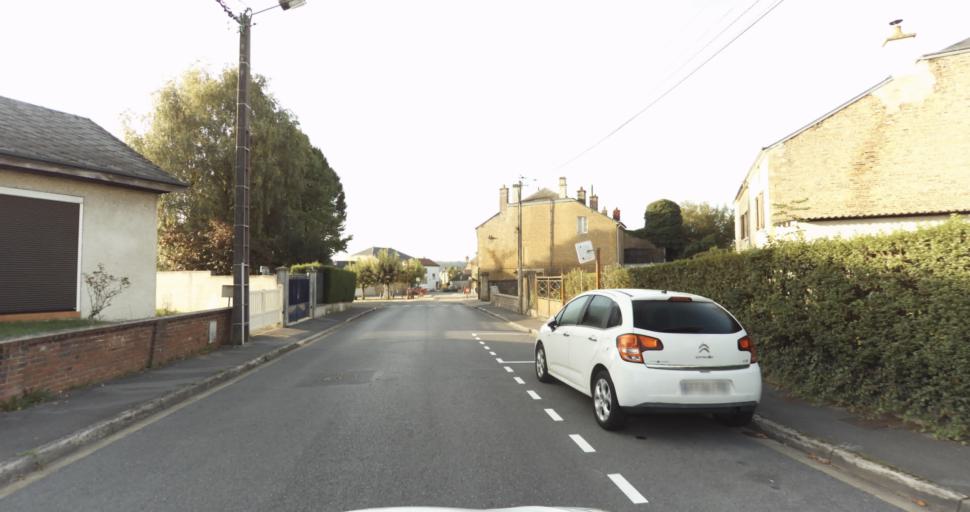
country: FR
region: Champagne-Ardenne
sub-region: Departement des Ardennes
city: Villers-Semeuse
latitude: 49.7404
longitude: 4.7485
